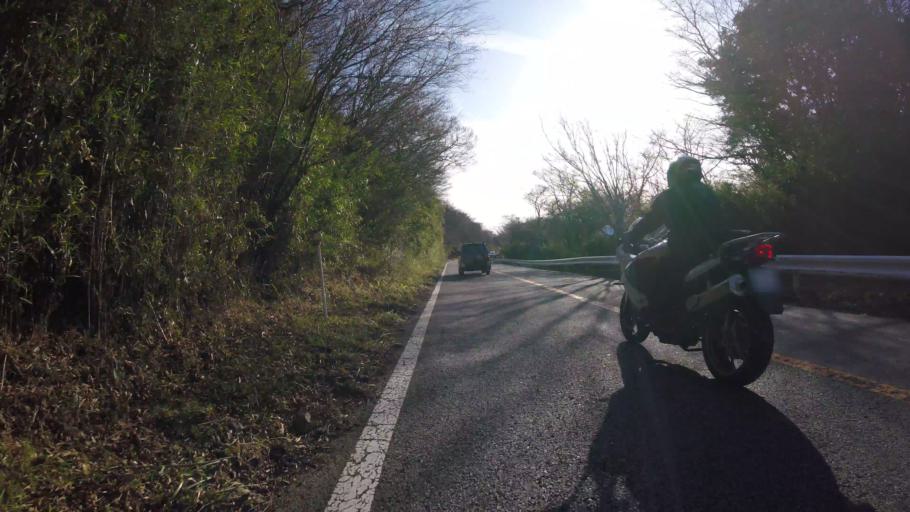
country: JP
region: Kanagawa
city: Hakone
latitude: 35.1558
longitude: 139.0260
